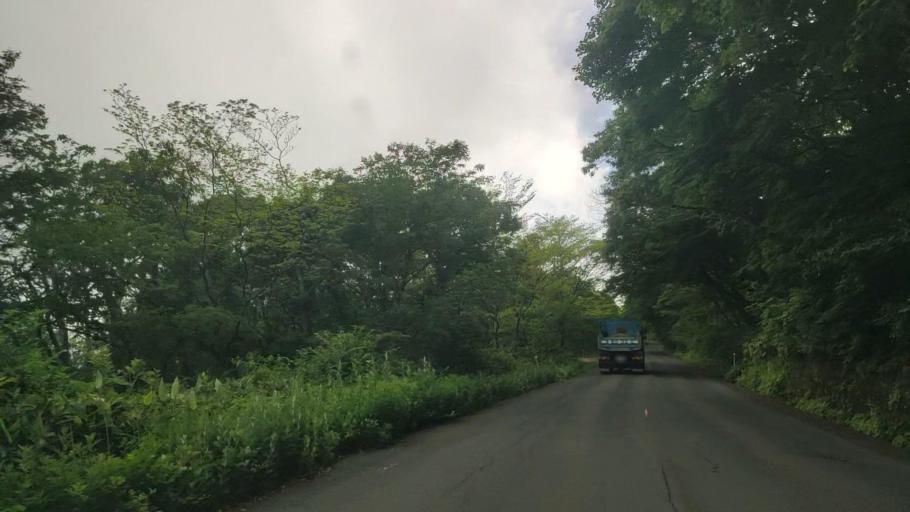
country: JP
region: Tottori
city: Yonago
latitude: 35.3799
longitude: 133.5213
